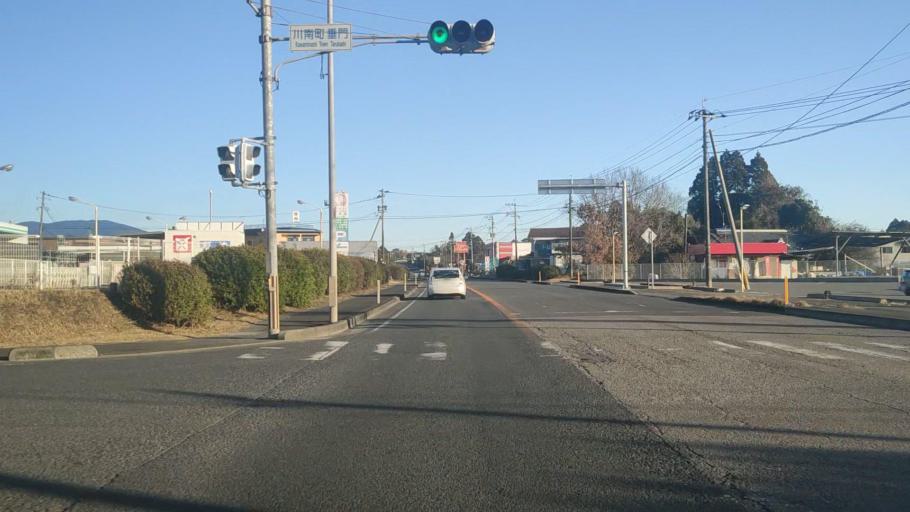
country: JP
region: Miyazaki
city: Takanabe
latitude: 32.1873
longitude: 131.5235
